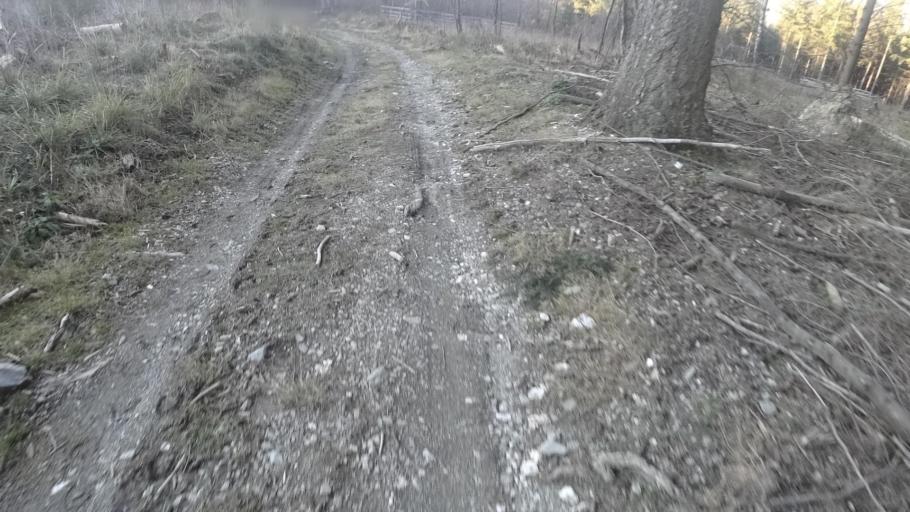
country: DE
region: Rheinland-Pfalz
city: Kamp-Bornhofen
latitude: 50.2020
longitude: 7.5927
